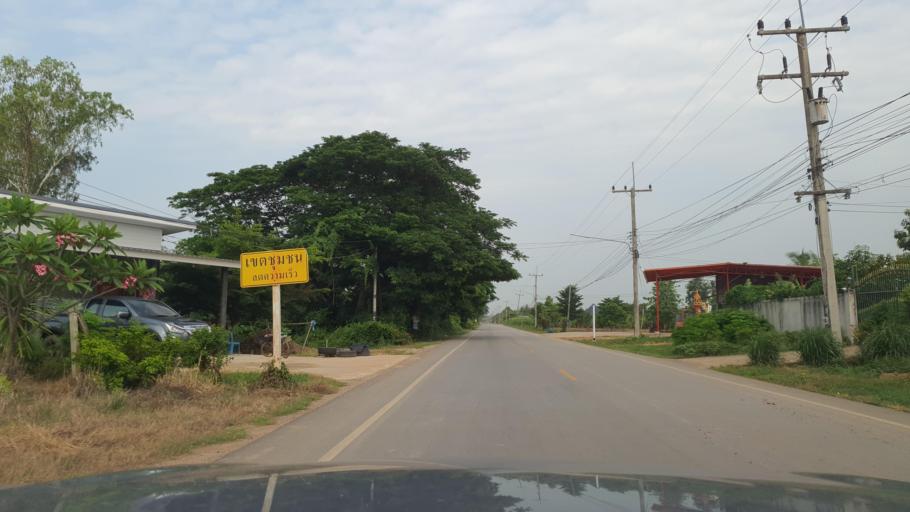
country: TH
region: Phitsanulok
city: Phitsanulok
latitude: 16.8148
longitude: 100.1791
